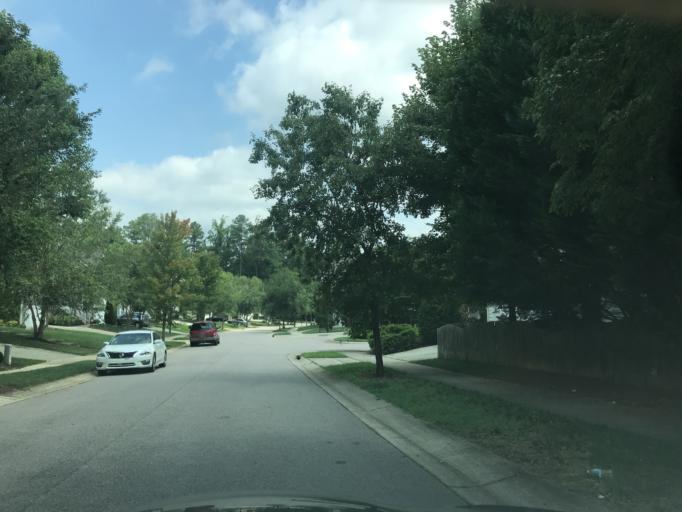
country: US
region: North Carolina
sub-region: Wake County
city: Wake Forest
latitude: 35.9290
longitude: -78.5750
